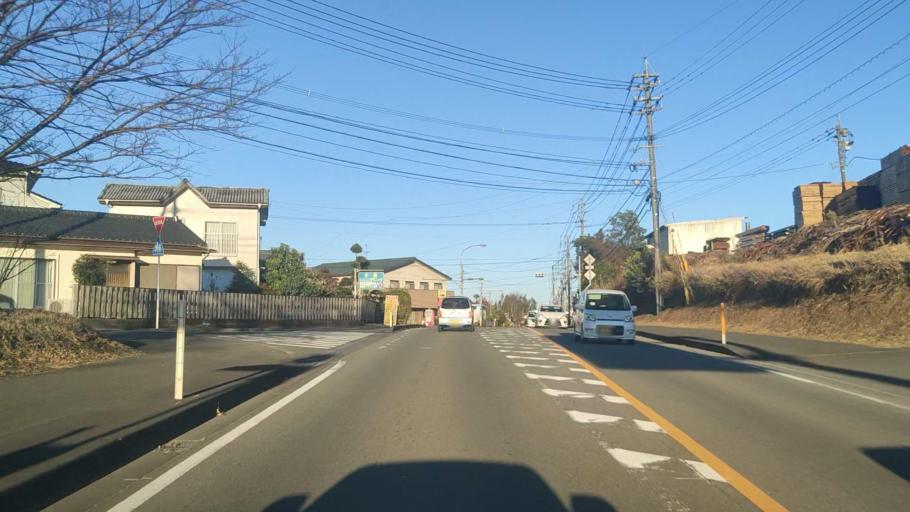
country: JP
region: Miyazaki
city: Miyazaki-shi
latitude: 31.8326
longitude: 131.3190
